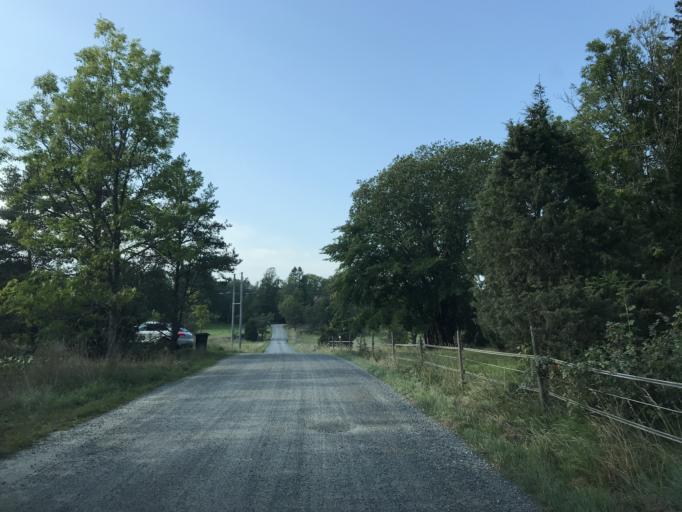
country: SE
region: Stockholm
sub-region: Norrtalje Kommun
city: Bjorko
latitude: 59.8492
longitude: 19.0142
